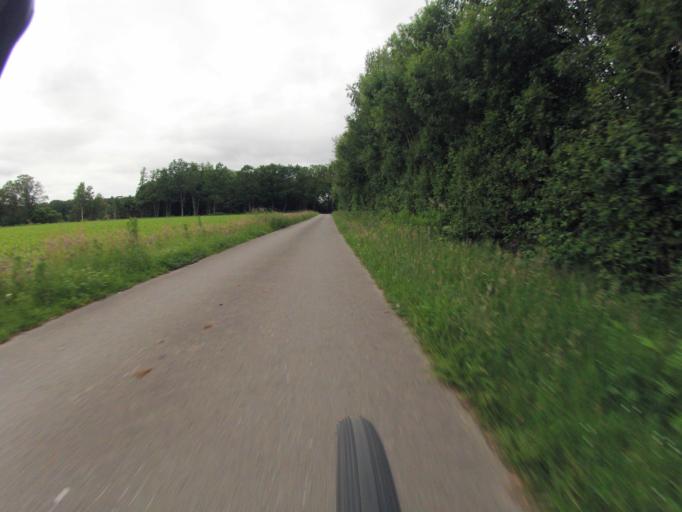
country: DE
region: North Rhine-Westphalia
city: Emsdetten
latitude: 52.2163
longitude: 7.5547
